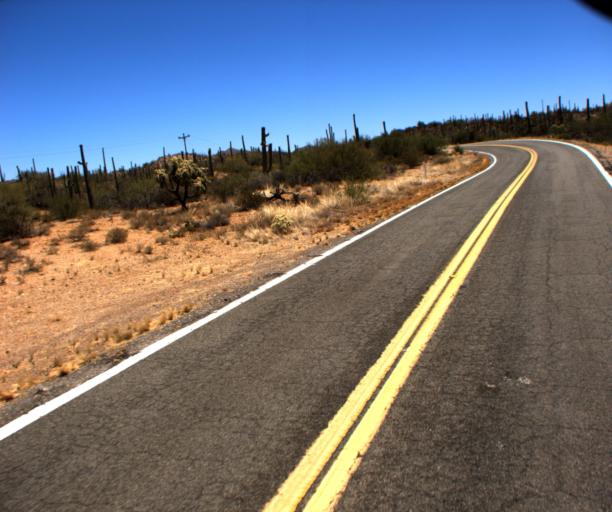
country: US
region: Arizona
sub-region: Pima County
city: Sells
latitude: 32.1736
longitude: -112.2024
